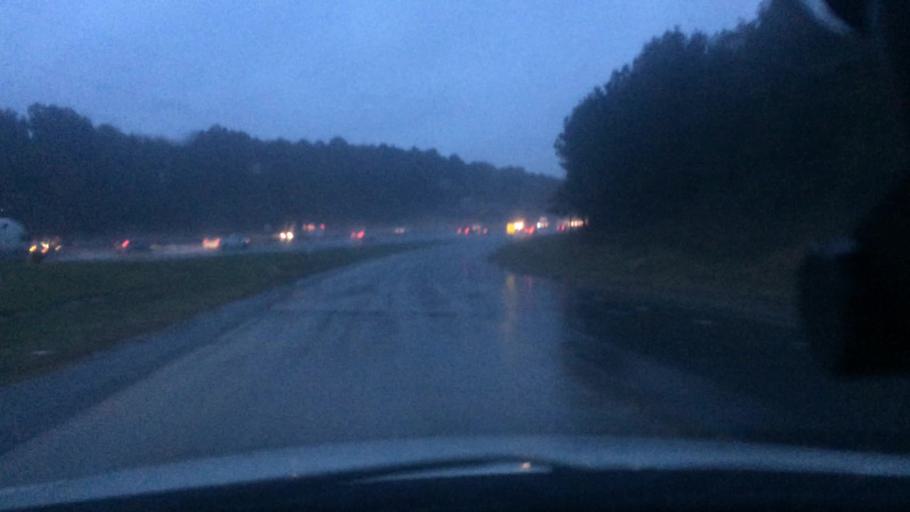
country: US
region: North Carolina
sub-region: Orange County
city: Chapel Hill
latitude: 35.9118
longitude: -78.9819
